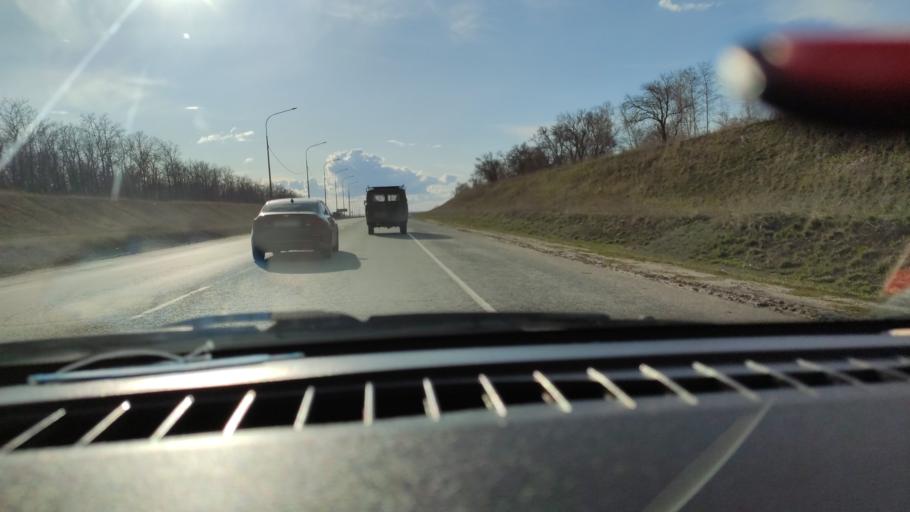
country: RU
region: Saratov
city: Yelshanka
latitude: 51.8247
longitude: 46.2999
